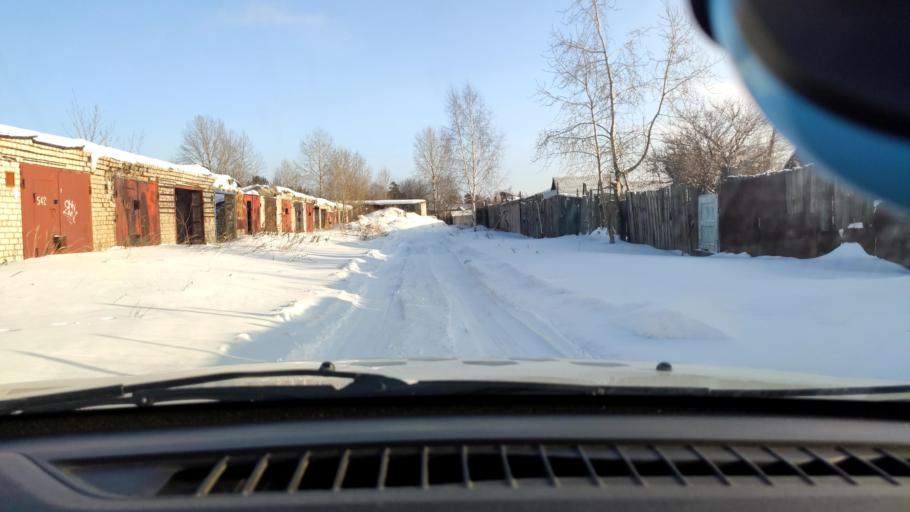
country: RU
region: Perm
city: Overyata
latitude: 58.0175
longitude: 55.9372
